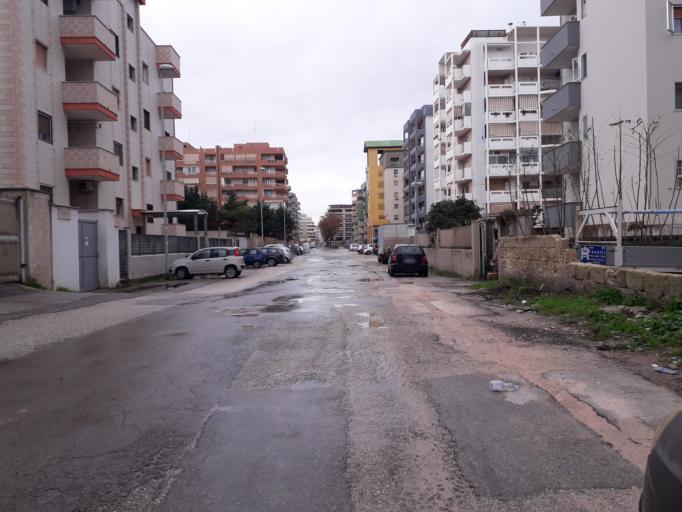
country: IT
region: Apulia
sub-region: Provincia di Bari
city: San Paolo
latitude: 41.1377
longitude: 16.8202
